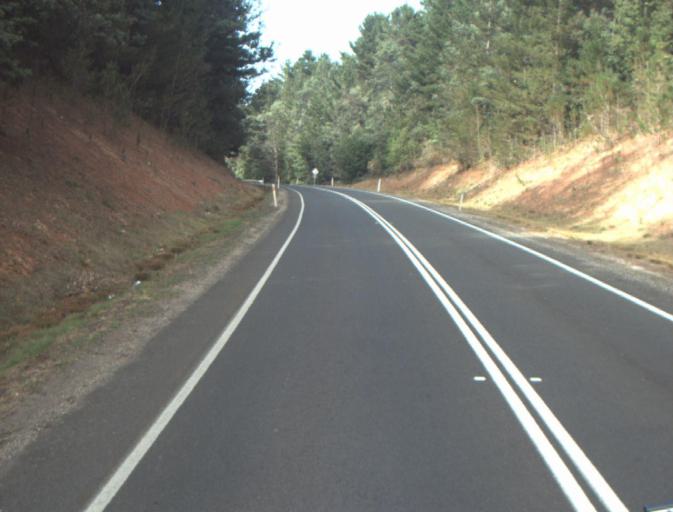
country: AU
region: Tasmania
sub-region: Launceston
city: Mayfield
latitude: -41.3012
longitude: 147.2061
